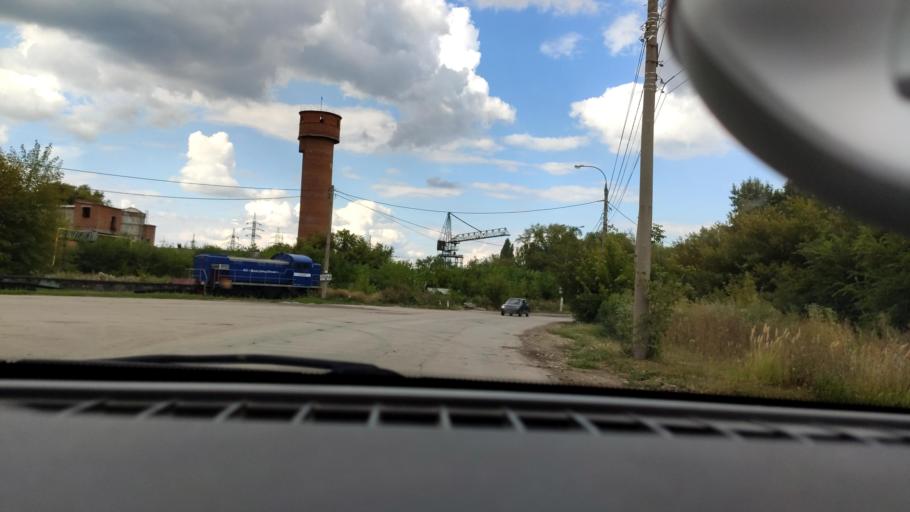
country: RU
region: Samara
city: Novokuybyshevsk
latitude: 53.1086
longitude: 50.0417
